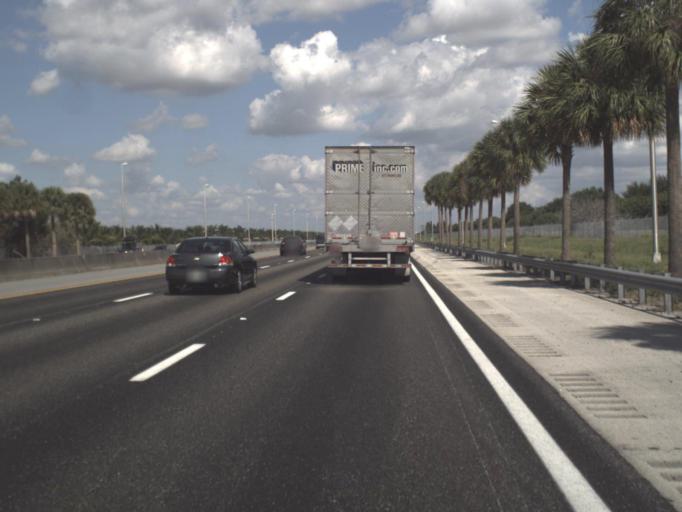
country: US
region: Florida
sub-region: Palm Beach County
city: Villages of Oriole
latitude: 26.5014
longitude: -80.1724
